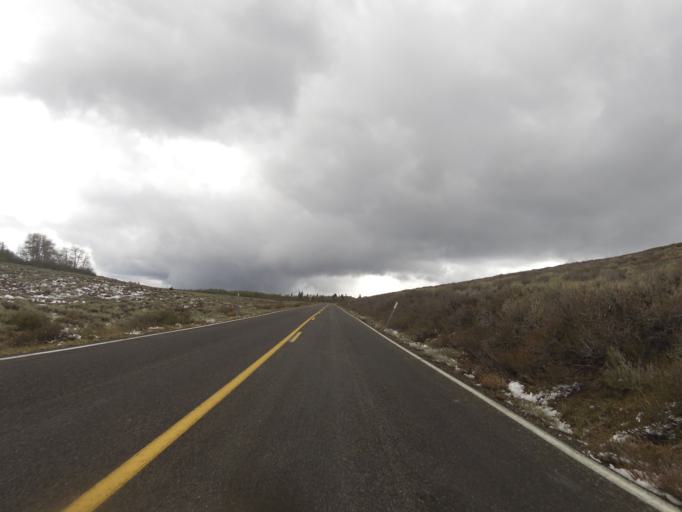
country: US
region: Nevada
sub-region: Douglas County
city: Gardnerville Ranchos
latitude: 38.6739
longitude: -119.6111
